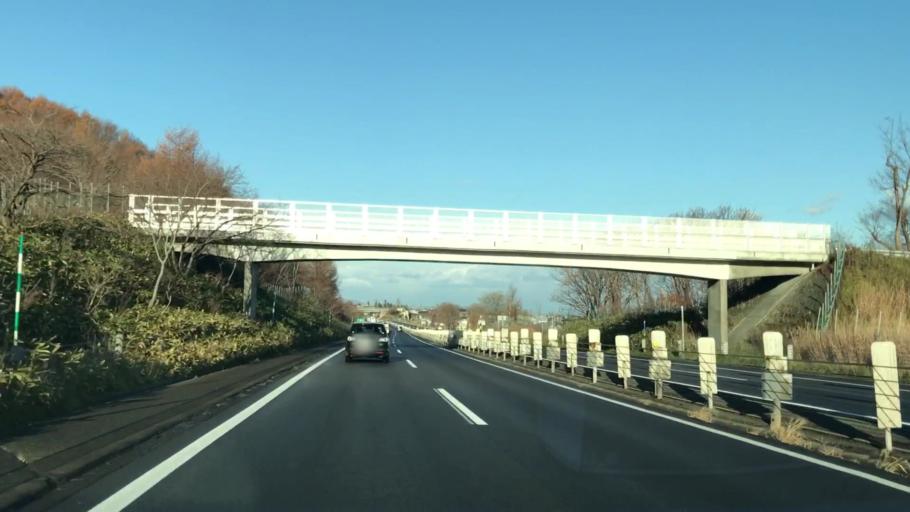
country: JP
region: Hokkaido
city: Sapporo
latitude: 43.1207
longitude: 141.2191
